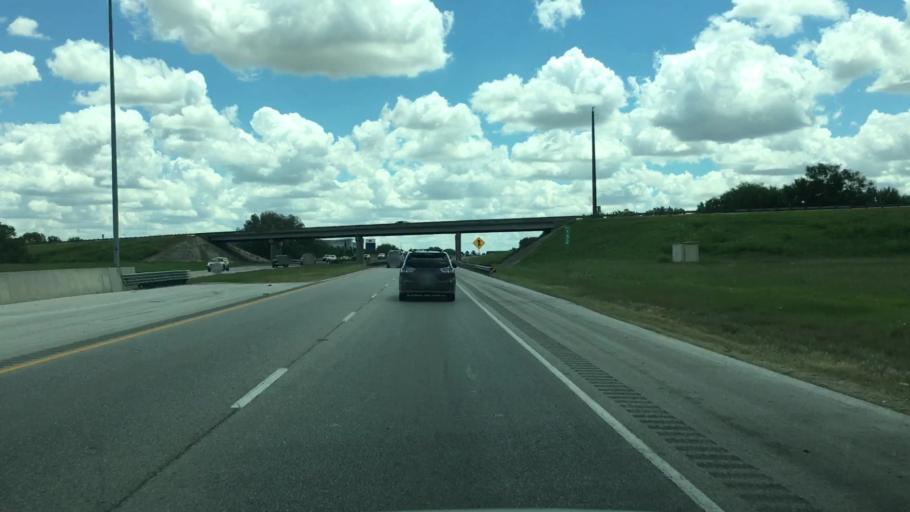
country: US
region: Texas
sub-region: Bexar County
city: Elmendorf
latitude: 29.3086
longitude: -98.4007
